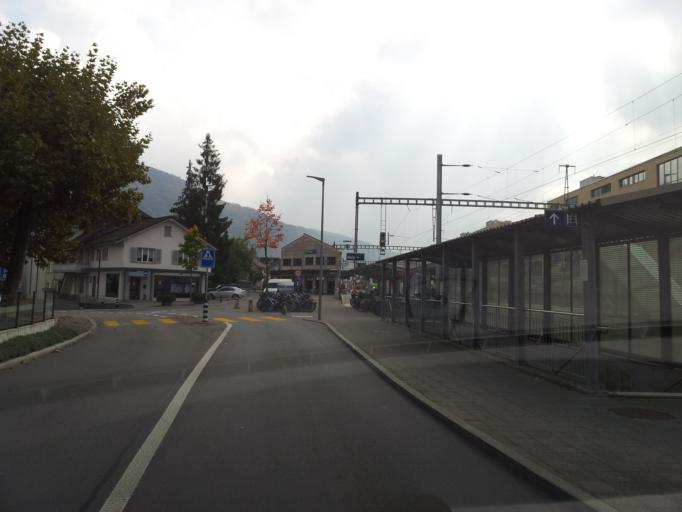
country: CH
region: Bern
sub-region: Bern-Mittelland District
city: Belp
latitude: 46.8901
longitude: 7.4980
